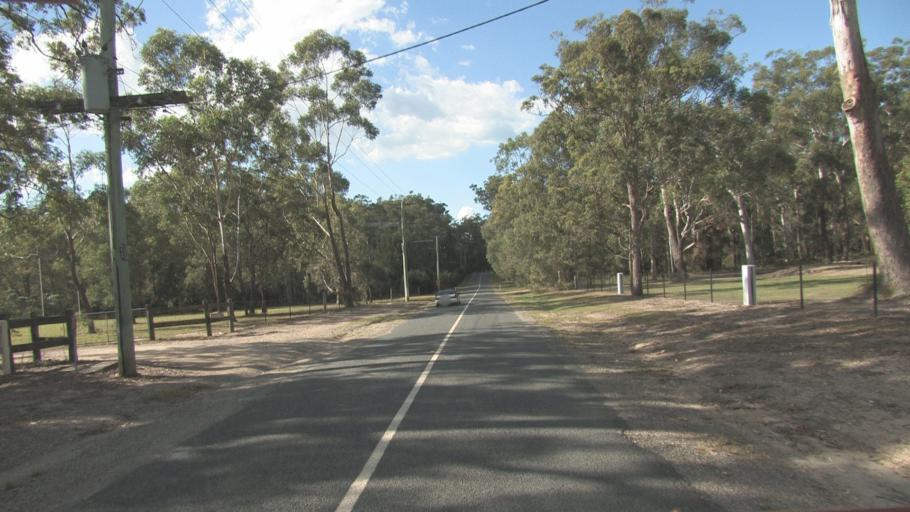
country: AU
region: Queensland
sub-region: Gold Coast
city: Yatala
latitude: -27.6567
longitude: 153.2457
